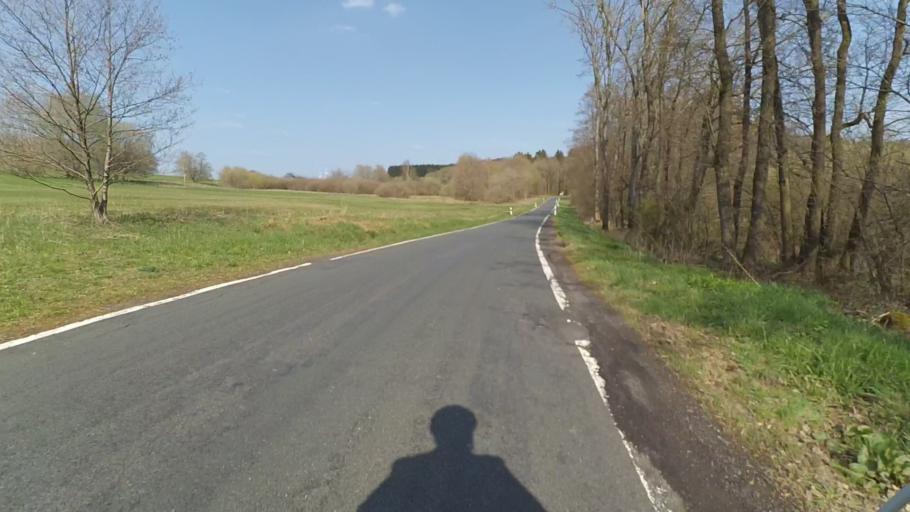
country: DE
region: Rheinland-Pfalz
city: Dreifelden
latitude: 50.6016
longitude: 7.8174
